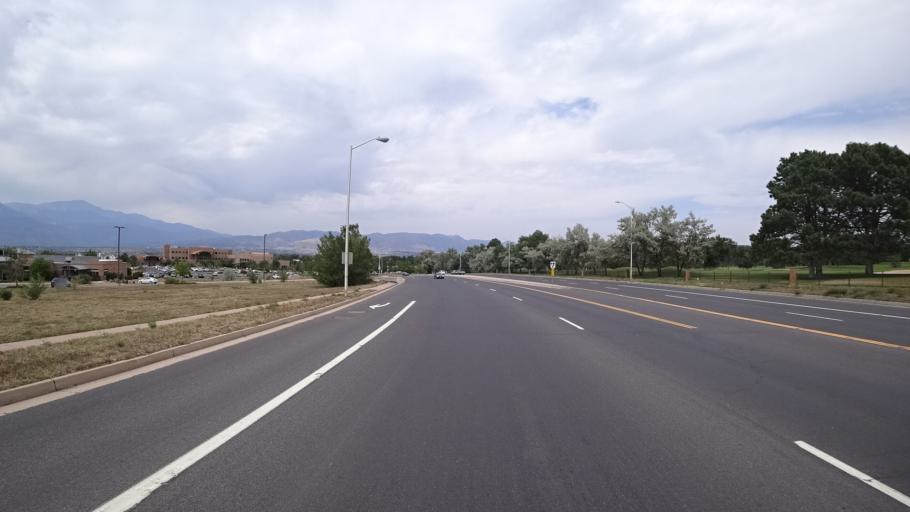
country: US
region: Colorado
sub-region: El Paso County
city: Colorado Springs
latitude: 38.8727
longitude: -104.7903
